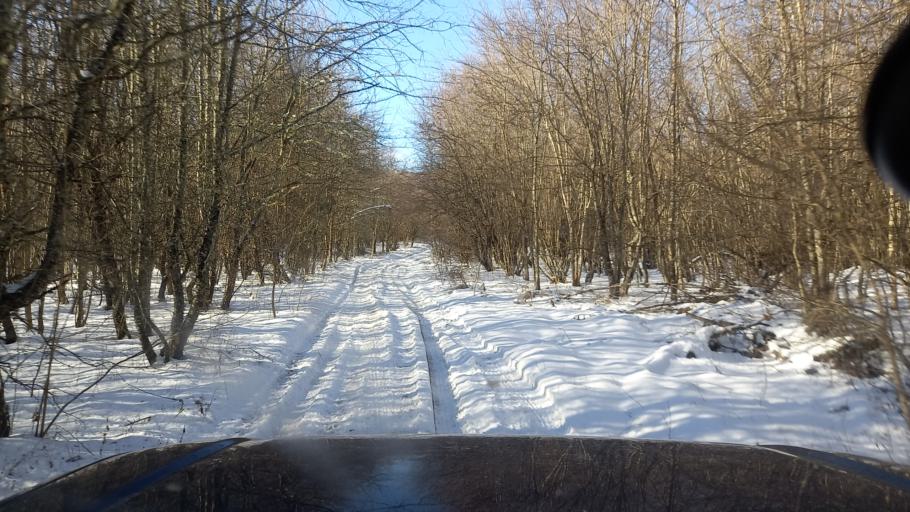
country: RU
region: Adygeya
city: Kamennomostskiy
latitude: 44.2108
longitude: 40.1430
